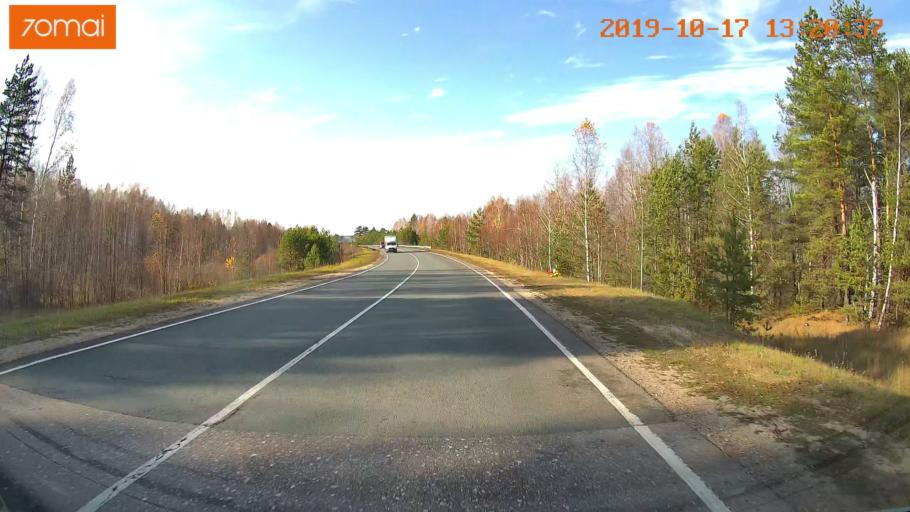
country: RU
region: Rjazan
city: Gus'-Zheleznyy
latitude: 55.0774
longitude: 41.0465
